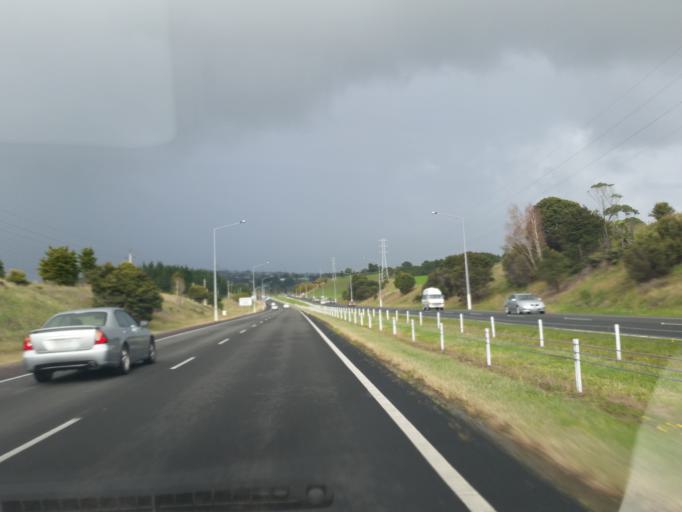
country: NZ
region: Auckland
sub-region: Auckland
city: Pukekohe East
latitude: -37.1562
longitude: 174.9775
